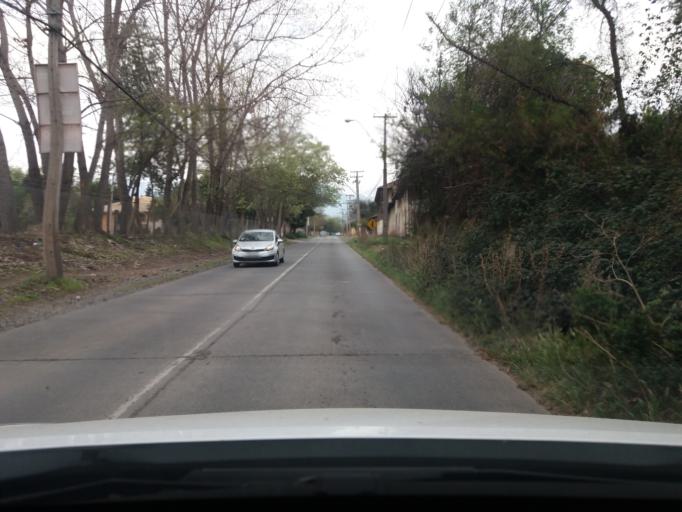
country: CL
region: Valparaiso
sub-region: Provincia de Los Andes
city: Los Andes
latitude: -32.8317
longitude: -70.6194
